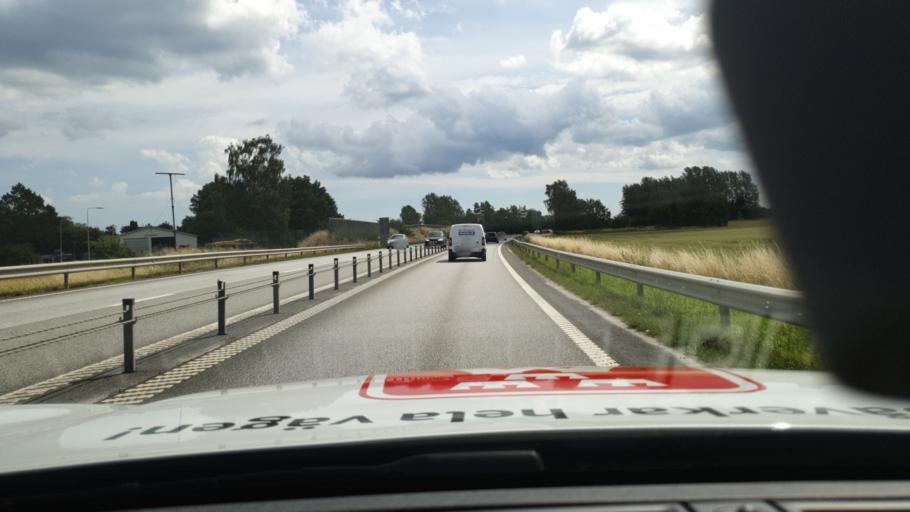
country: SE
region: Skane
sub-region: Kristianstads Kommun
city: Kristianstad
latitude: 56.0249
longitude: 14.0983
